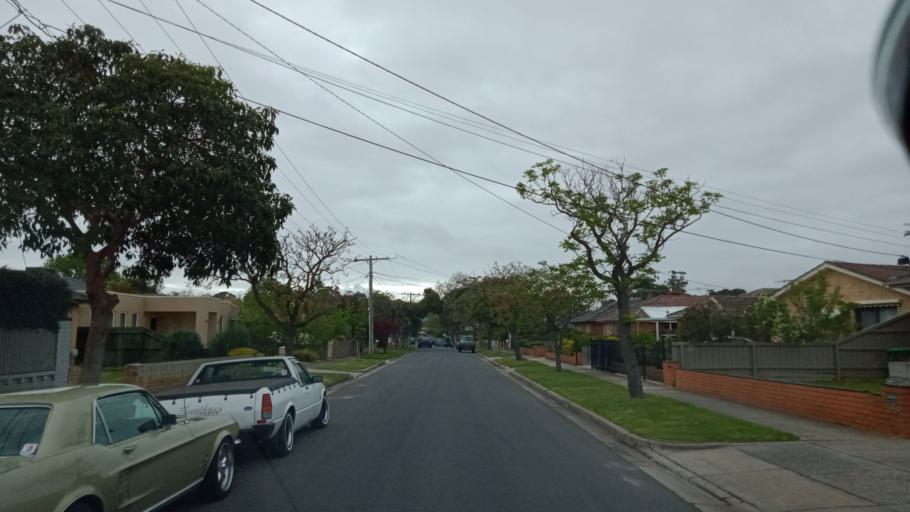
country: AU
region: Victoria
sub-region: Monash
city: Oakleigh South
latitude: -37.9316
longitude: 145.0705
